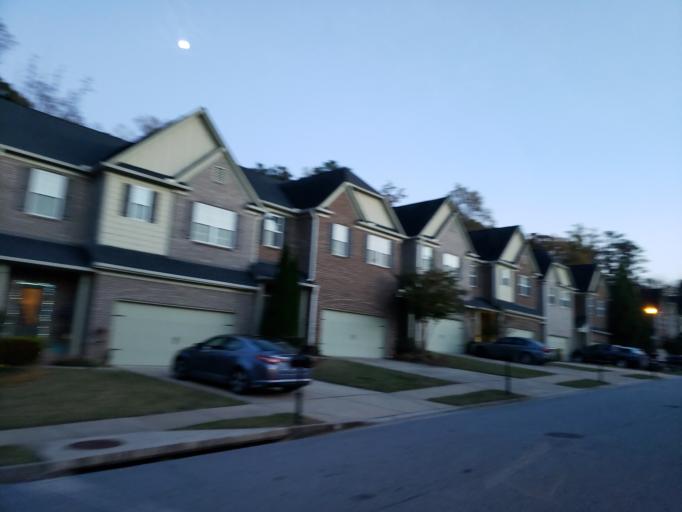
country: US
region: Georgia
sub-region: DeKalb County
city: Chamblee
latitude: 33.8960
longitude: -84.3203
